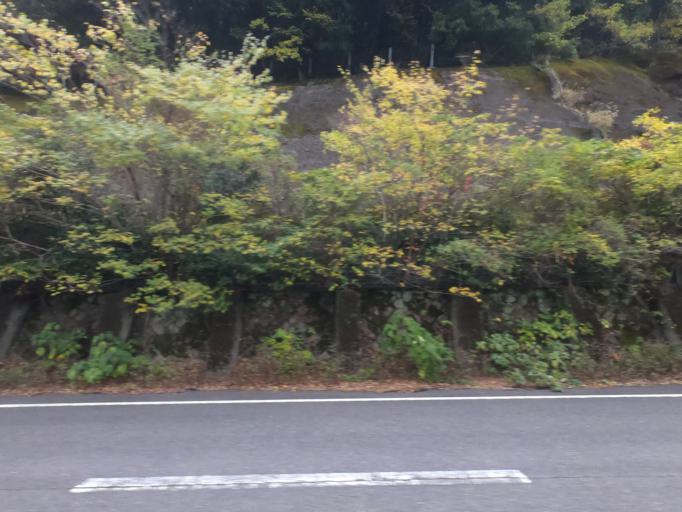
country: JP
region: Kumamoto
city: Minamata
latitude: 32.2427
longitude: 130.4844
